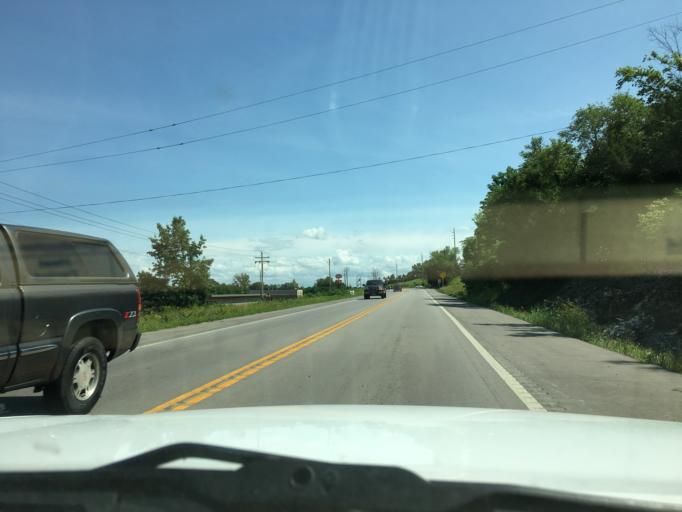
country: US
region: Missouri
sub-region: Franklin County
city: Union
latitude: 38.4631
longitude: -91.0051
